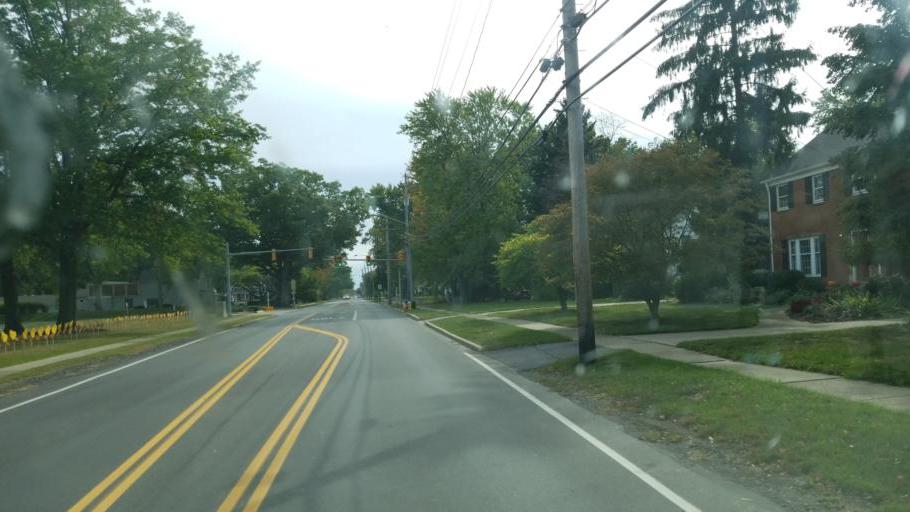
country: US
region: Ohio
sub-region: Lorain County
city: Avon Lake
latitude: 41.5076
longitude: -82.0187
